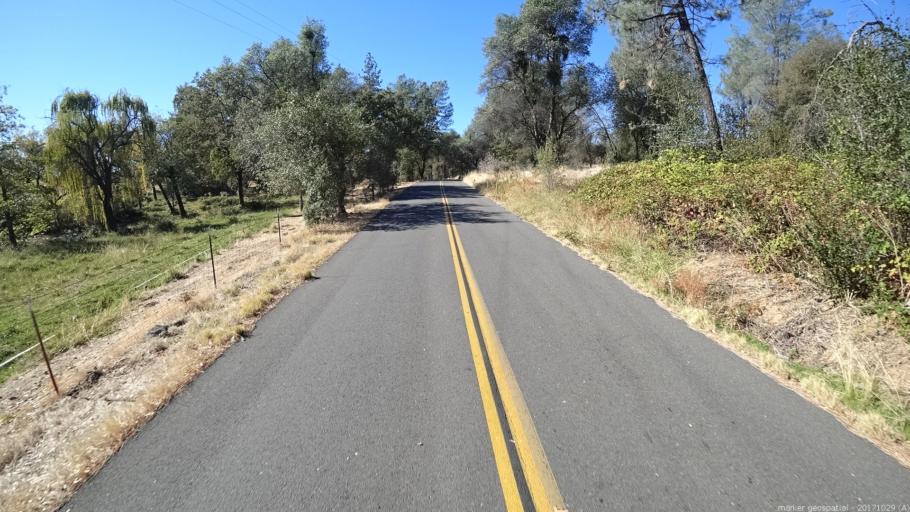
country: US
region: California
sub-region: Shasta County
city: Shasta
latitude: 40.4816
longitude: -122.6394
